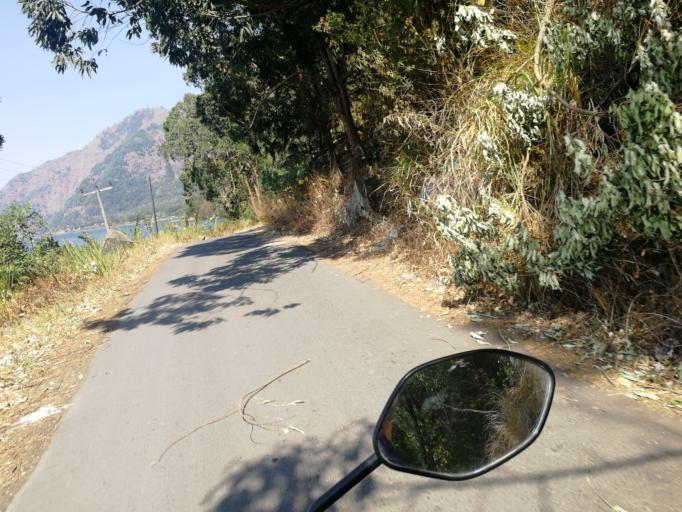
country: ID
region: Bali
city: Banjar Buahan
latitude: -8.2874
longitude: 115.3965
